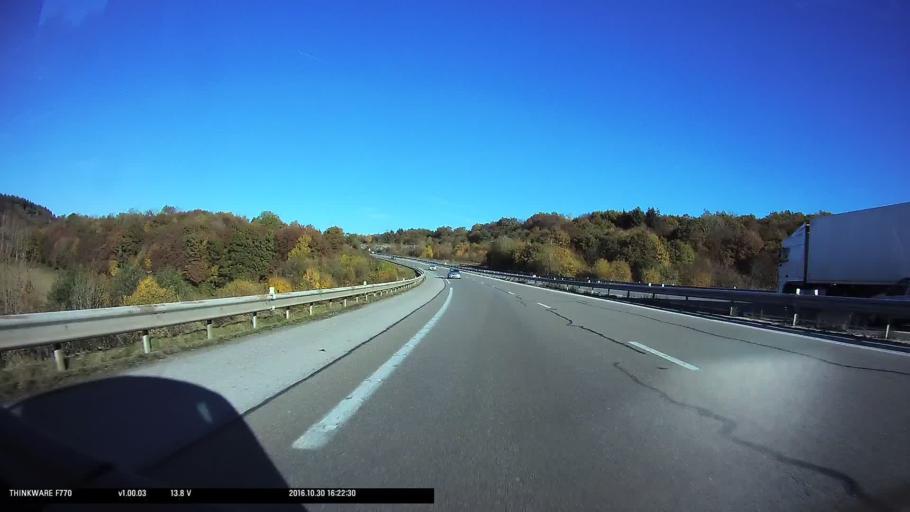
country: FR
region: Franche-Comte
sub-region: Departement du Doubs
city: Baume-les-Dames
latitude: 47.3834
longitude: 6.4215
